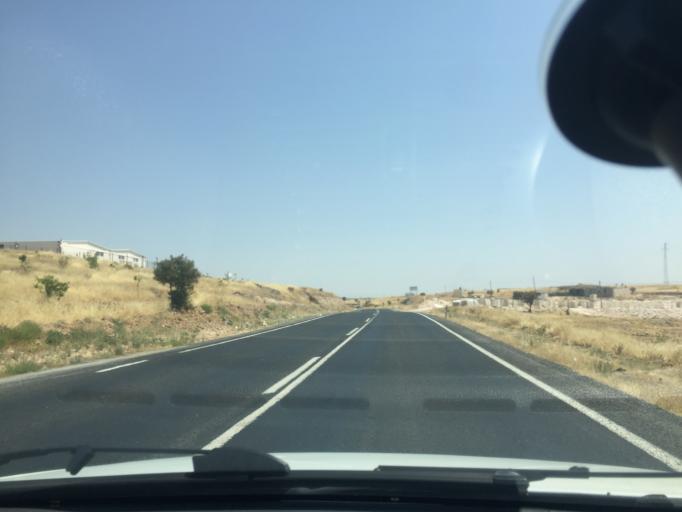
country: TR
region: Mardin
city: Kindirip
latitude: 37.4559
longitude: 41.2460
